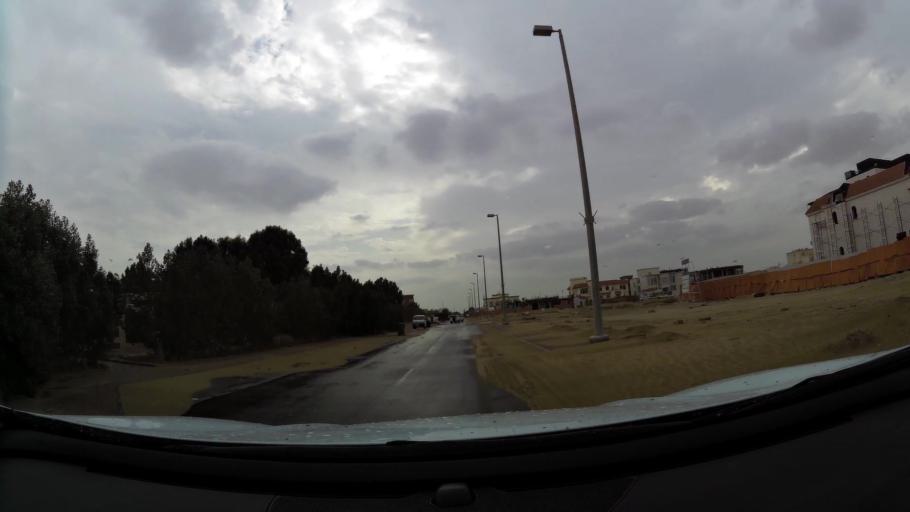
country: AE
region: Abu Dhabi
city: Abu Dhabi
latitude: 24.3645
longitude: 54.6249
